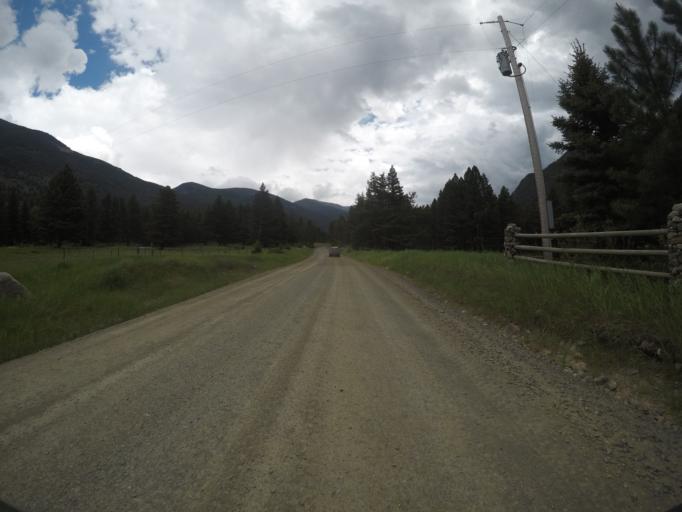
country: US
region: Montana
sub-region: Park County
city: Livingston
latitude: 45.4805
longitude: -110.2106
